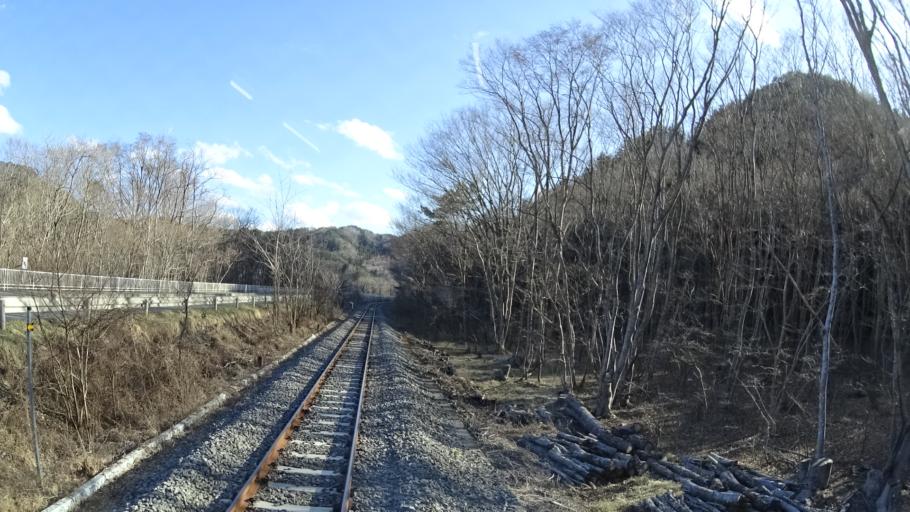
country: JP
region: Iwate
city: Yamada
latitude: 39.5490
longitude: 141.9390
